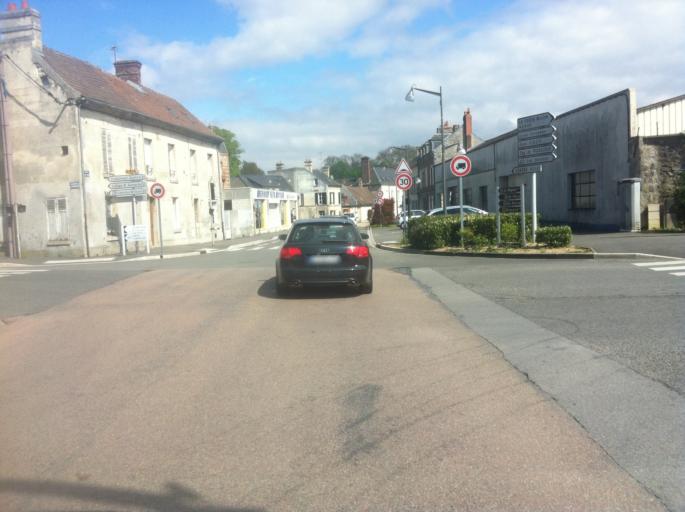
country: FR
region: Picardie
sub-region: Departement de l'Aisne
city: Villers-Cotterets
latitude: 49.2558
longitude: 3.0844
